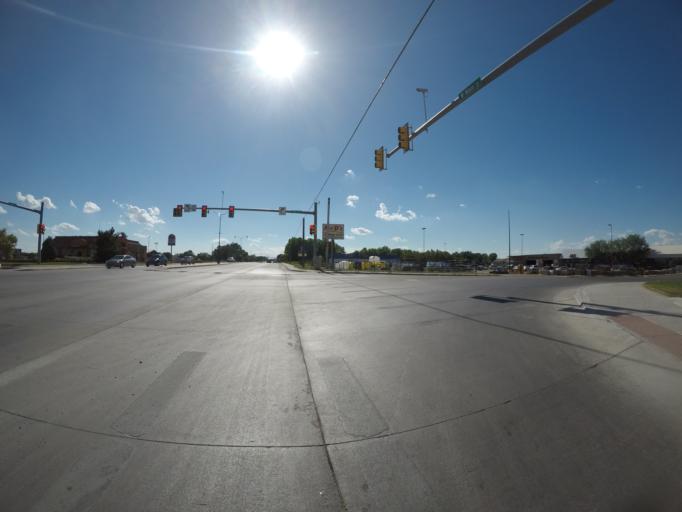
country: US
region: Colorado
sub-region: Logan County
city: Sterling
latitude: 40.6253
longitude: -103.2311
